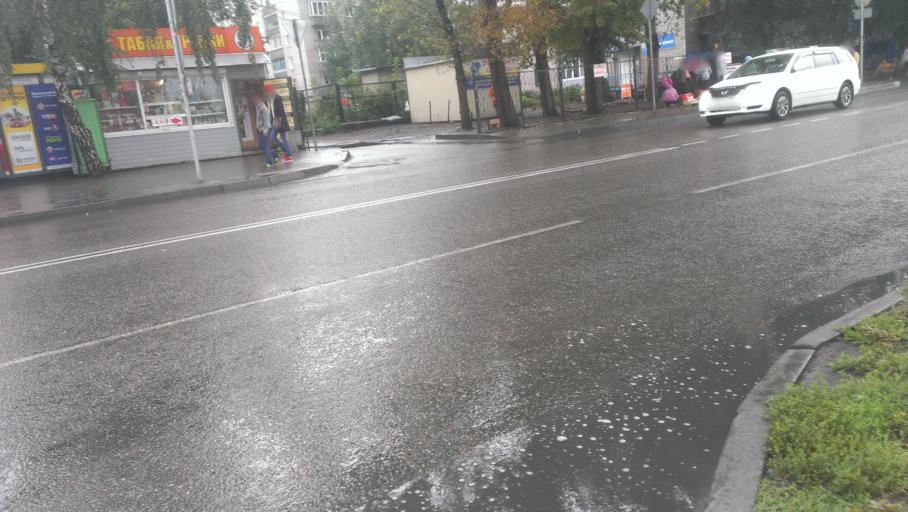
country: RU
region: Altai Krai
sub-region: Gorod Barnaulskiy
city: Barnaul
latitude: 53.3616
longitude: 83.7645
